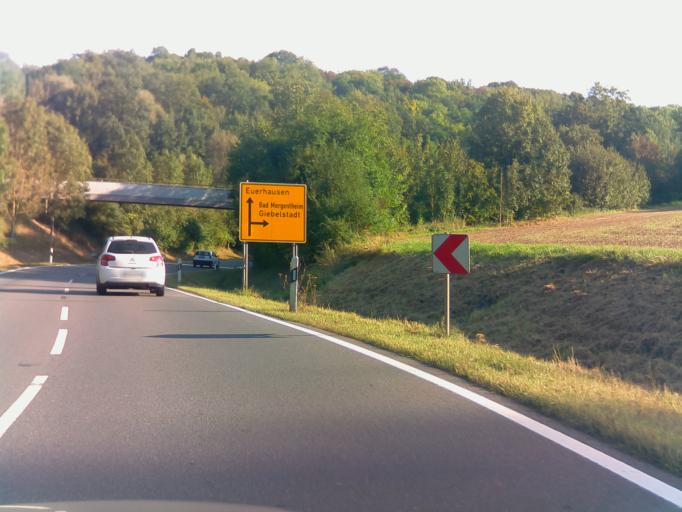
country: DE
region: Bavaria
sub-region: Regierungsbezirk Unterfranken
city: Gaukonigshofen
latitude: 49.6539
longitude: 10.0275
